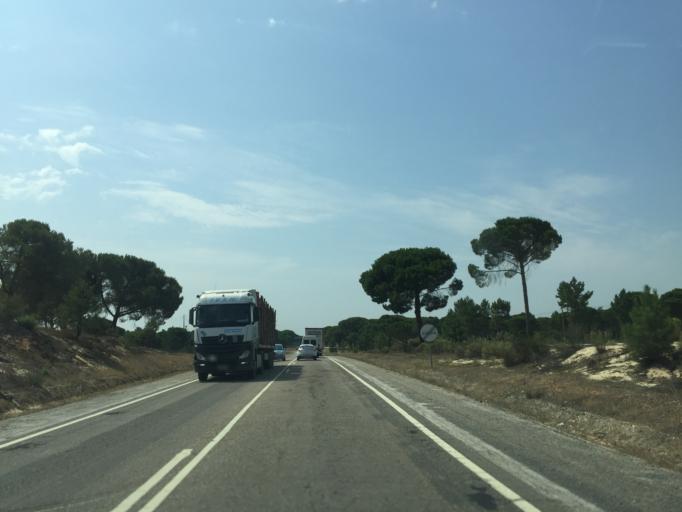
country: PT
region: Setubal
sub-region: Grandola
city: Grandola
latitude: 38.2733
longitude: -8.5409
